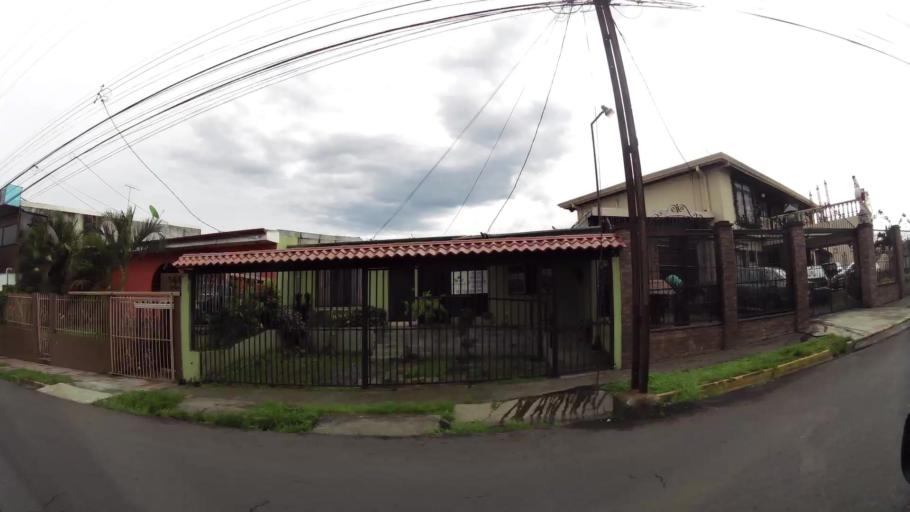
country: CR
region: San Jose
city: San Juan
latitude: 9.9629
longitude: -84.0862
